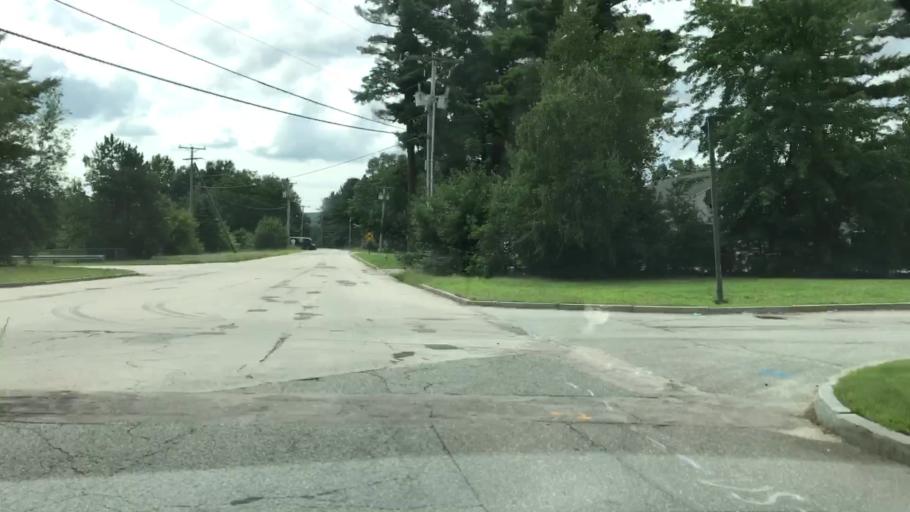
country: US
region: New Hampshire
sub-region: Hillsborough County
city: Hollis
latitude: 42.8108
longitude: -71.5830
